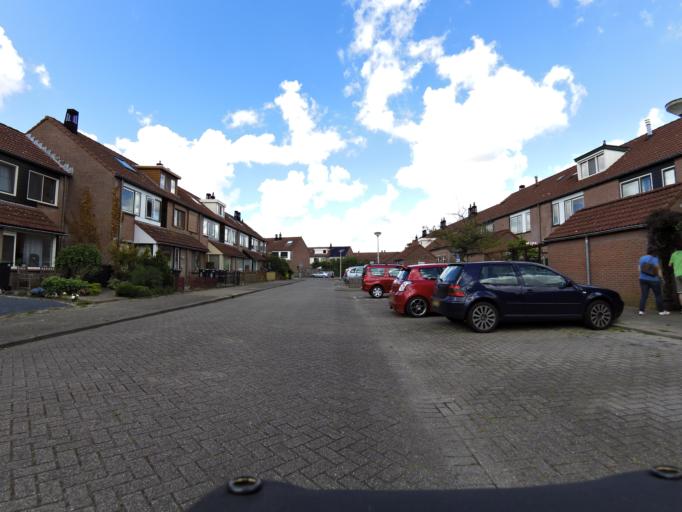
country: NL
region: South Holland
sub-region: Gemeente Hellevoetsluis
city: Hellevoetsluis
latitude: 51.8282
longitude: 4.1658
